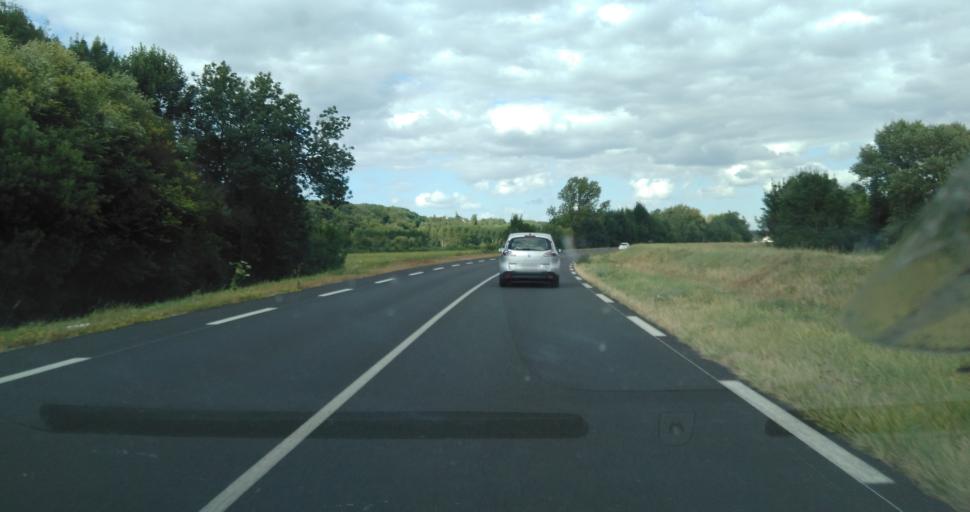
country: FR
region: Centre
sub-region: Departement d'Indre-et-Loire
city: Langeais
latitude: 47.2947
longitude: 0.3371
